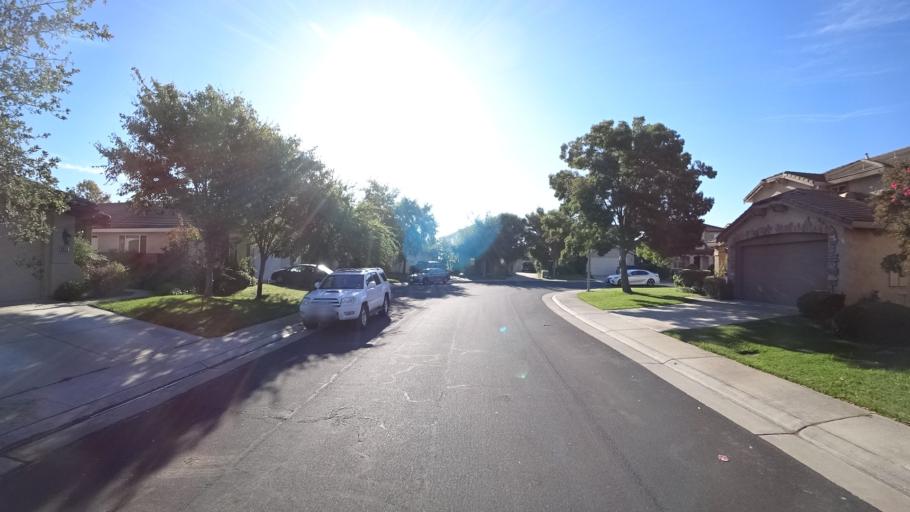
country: US
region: California
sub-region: Sacramento County
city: Laguna
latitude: 38.3998
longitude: -121.4660
